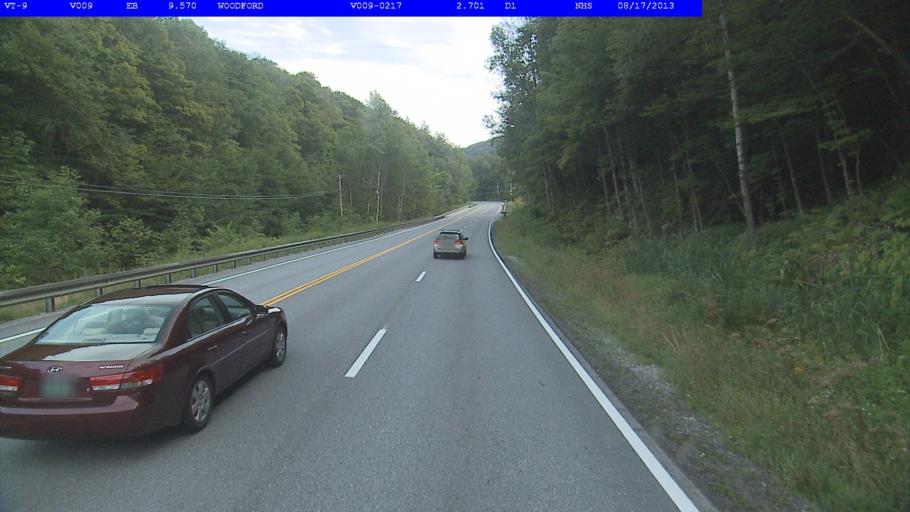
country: US
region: Vermont
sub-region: Bennington County
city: Bennington
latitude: 42.8822
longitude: -73.1162
